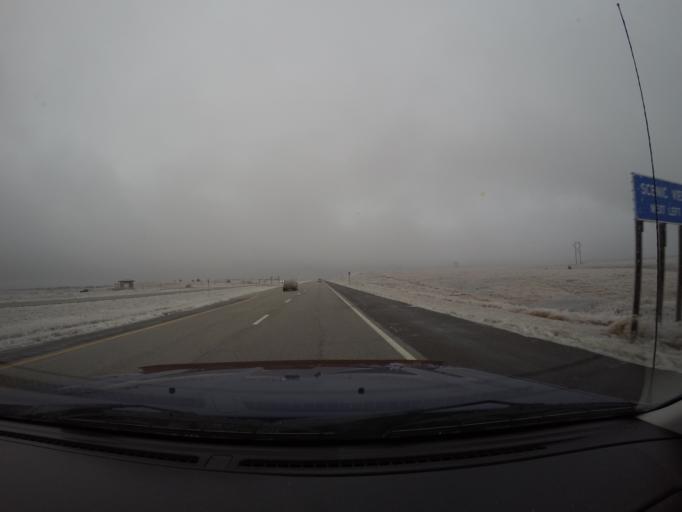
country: US
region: Kansas
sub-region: Riley County
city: Manhattan
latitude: 39.1312
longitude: -96.5380
